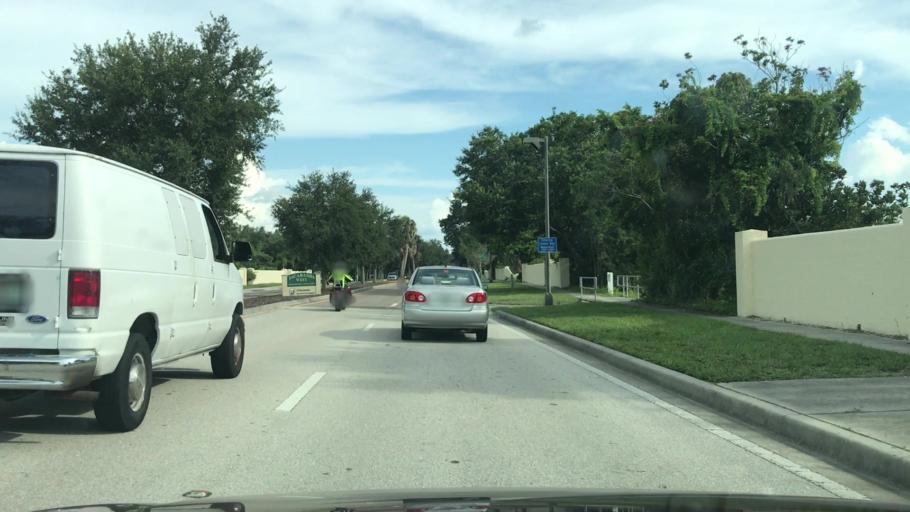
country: US
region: Florida
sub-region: Sarasota County
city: Plantation
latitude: 27.0777
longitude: -82.3890
